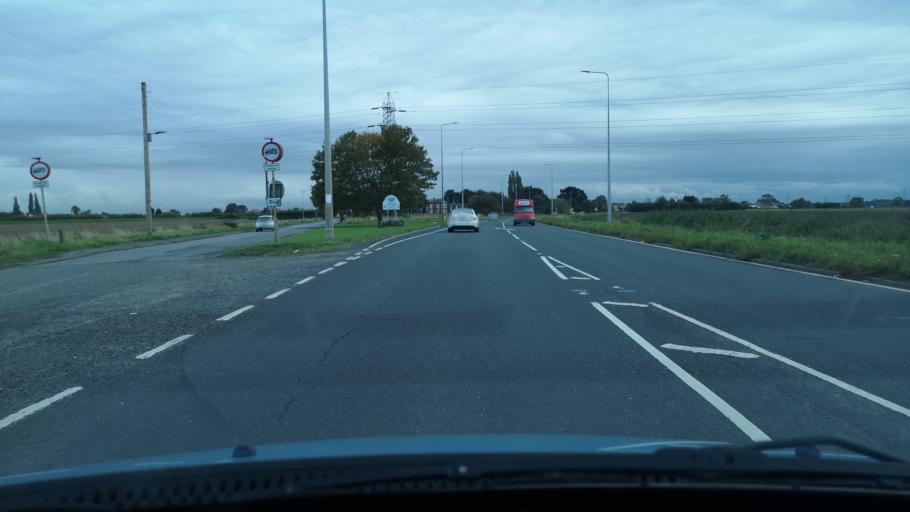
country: GB
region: England
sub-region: North Lincolnshire
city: Gunness
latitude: 53.5835
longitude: -0.7374
